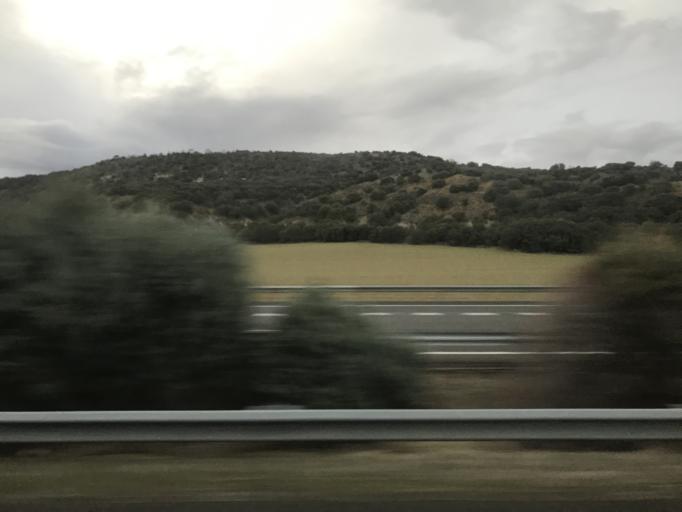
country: ES
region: Castille and Leon
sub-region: Provincia de Palencia
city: Quintana del Puente
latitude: 42.0921
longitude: -4.2087
